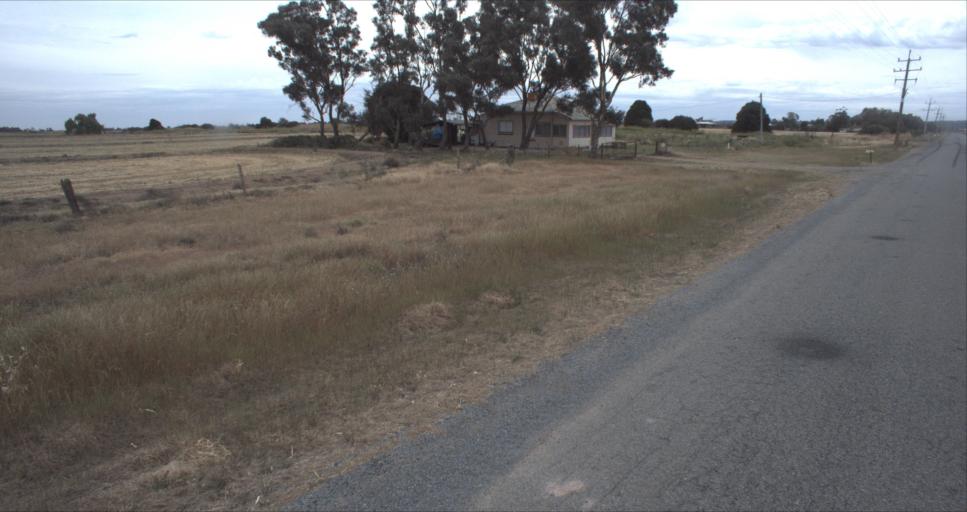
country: AU
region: New South Wales
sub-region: Leeton
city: Leeton
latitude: -34.4956
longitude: 146.4006
